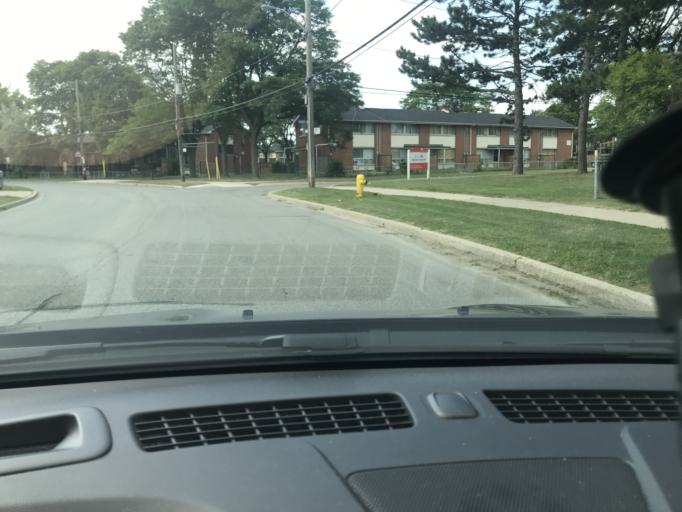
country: CA
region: Ontario
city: Toronto
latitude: 43.7224
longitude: -79.4415
